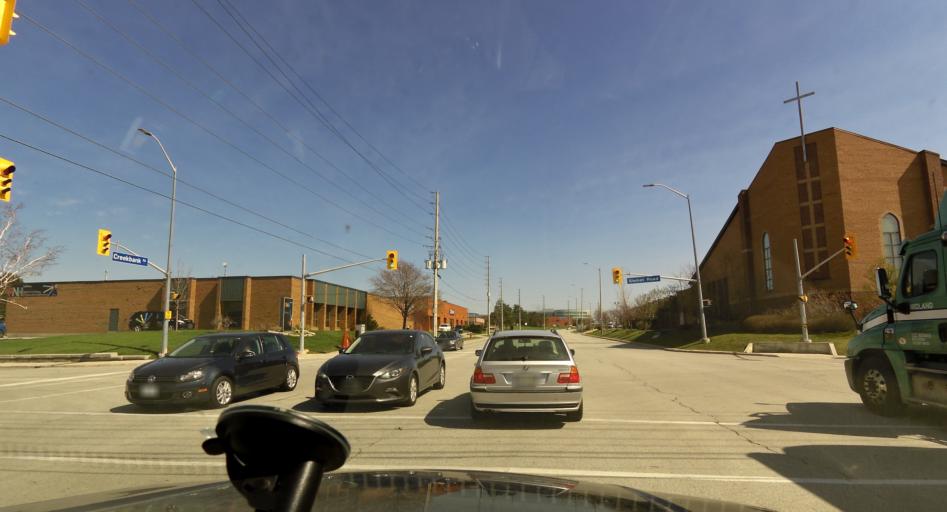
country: CA
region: Ontario
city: Etobicoke
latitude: 43.6476
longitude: -79.6196
